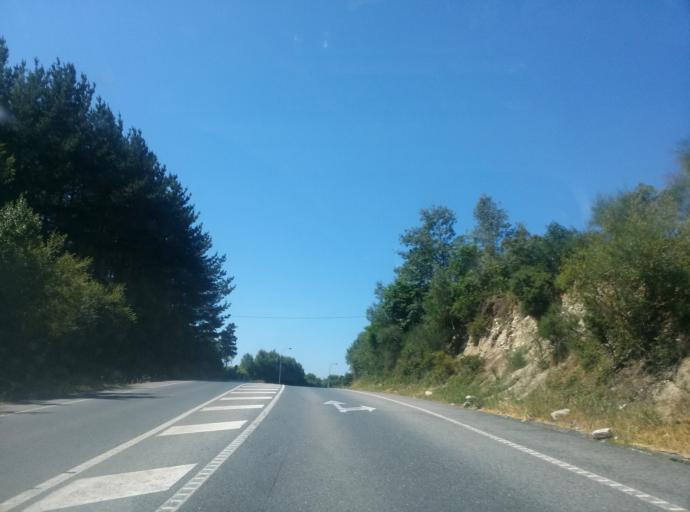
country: ES
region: Galicia
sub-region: Provincia de Lugo
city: Mos
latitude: 43.1260
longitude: -7.4866
